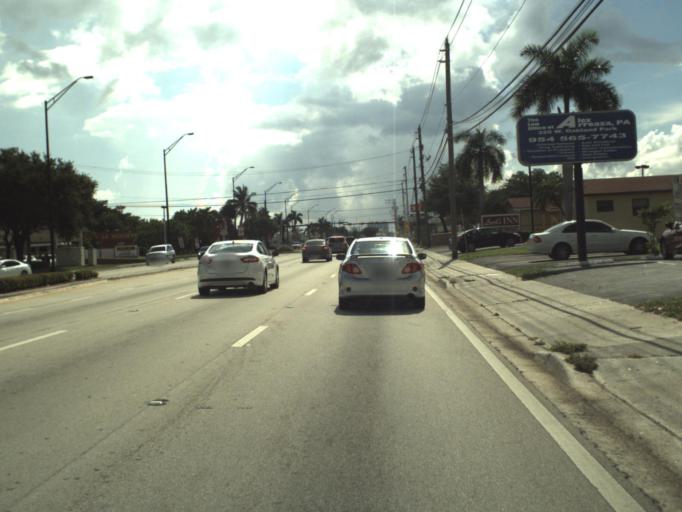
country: US
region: Florida
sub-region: Broward County
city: Wilton Manors
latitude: 26.1663
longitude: -80.1494
